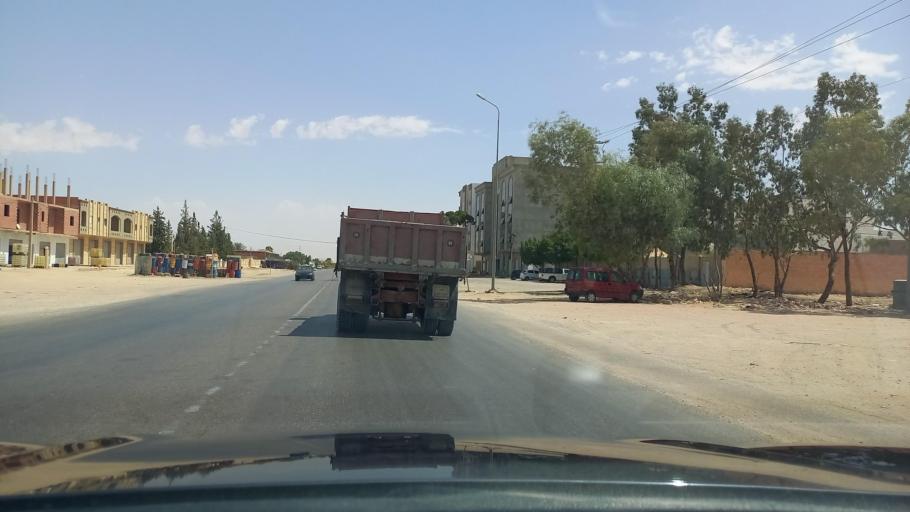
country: TN
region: Madanin
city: Medenine
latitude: 33.3649
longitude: 10.4598
